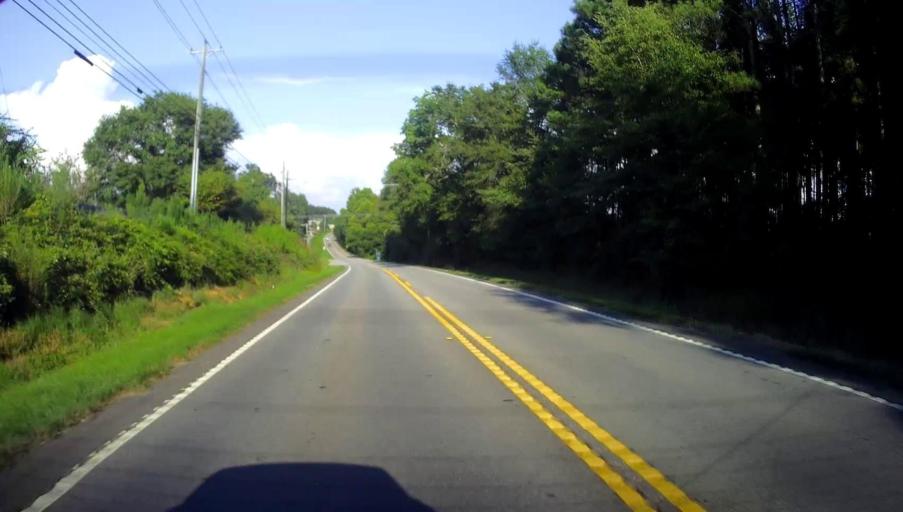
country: US
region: Georgia
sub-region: Houston County
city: Perry
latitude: 32.5061
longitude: -83.6465
